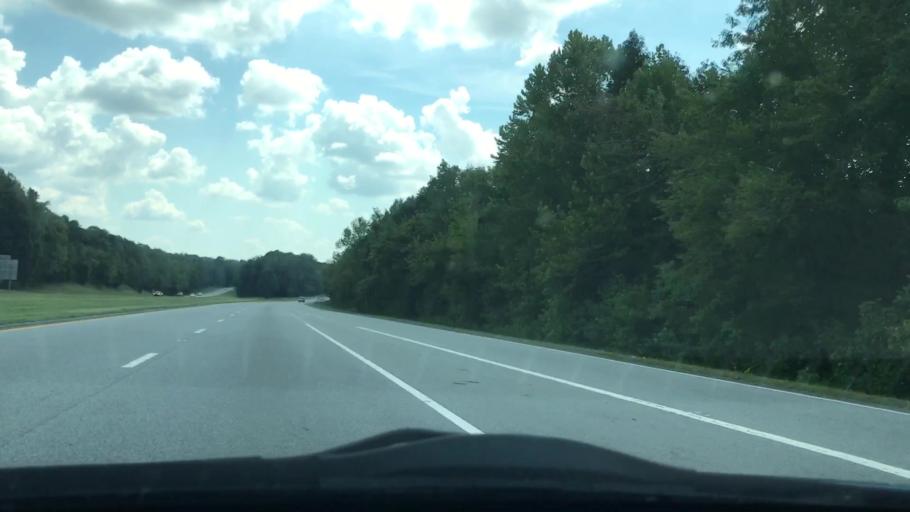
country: US
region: North Carolina
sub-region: Guilford County
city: Pleasant Garden
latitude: 35.9189
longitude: -79.8246
